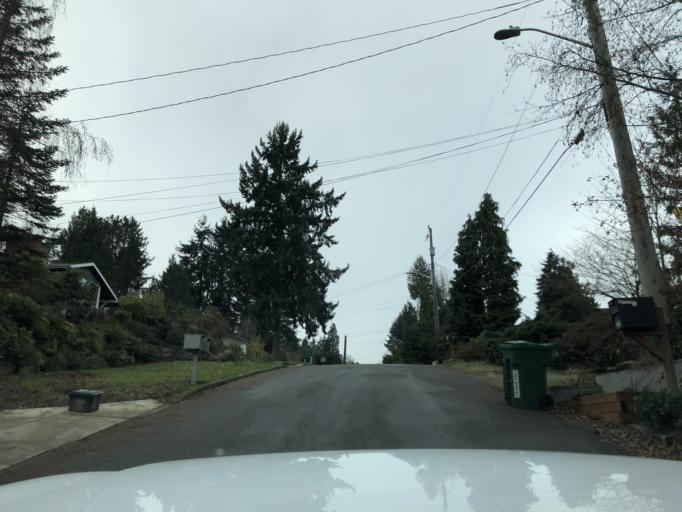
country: US
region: Washington
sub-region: King County
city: Lake Forest Park
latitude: 47.7009
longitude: -122.2866
